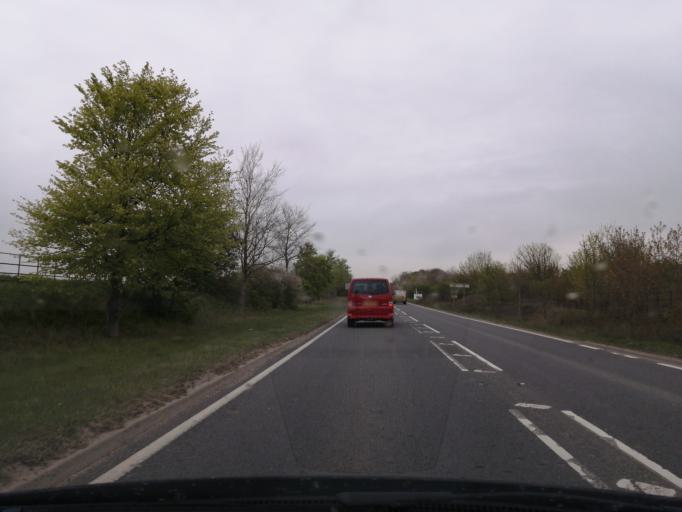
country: GB
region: England
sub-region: Peterborough
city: Thornhaugh
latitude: 52.5845
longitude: -0.4270
